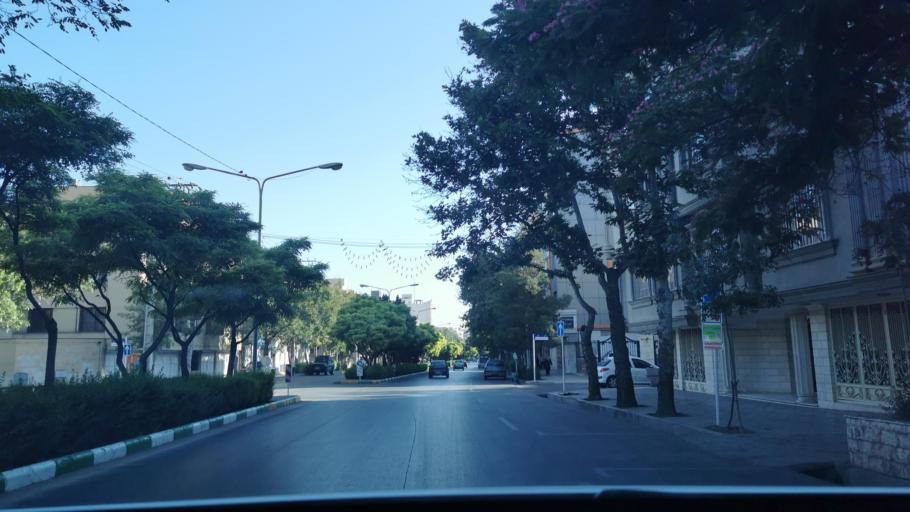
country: IR
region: Razavi Khorasan
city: Mashhad
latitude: 36.2935
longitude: 59.5679
